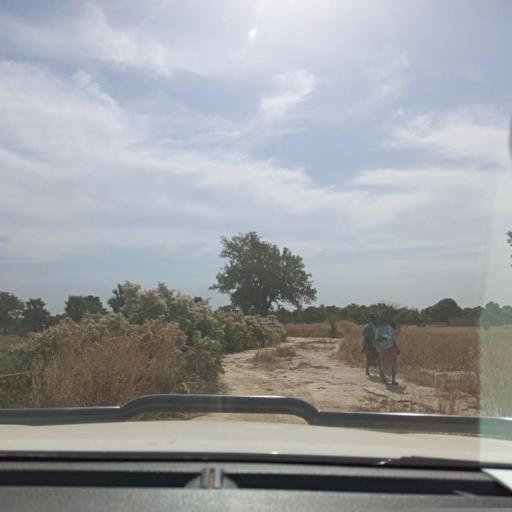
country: ML
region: Koulikoro
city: Kati
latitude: 12.7284
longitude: -8.2556
